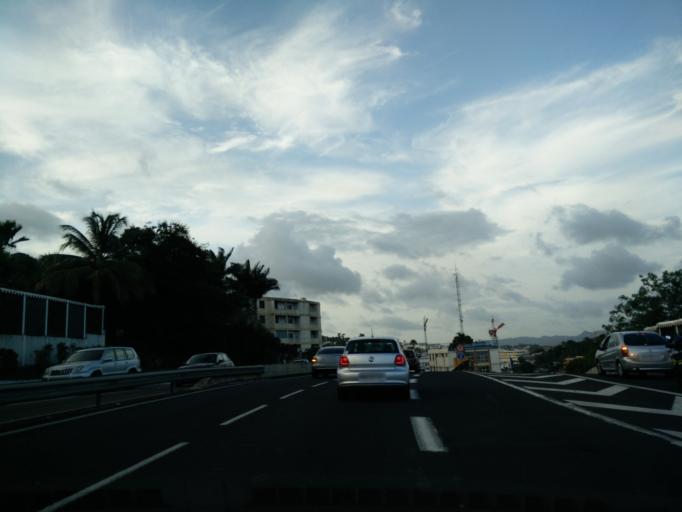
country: MQ
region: Martinique
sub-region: Martinique
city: Fort-de-France
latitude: 14.6132
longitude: -61.0649
